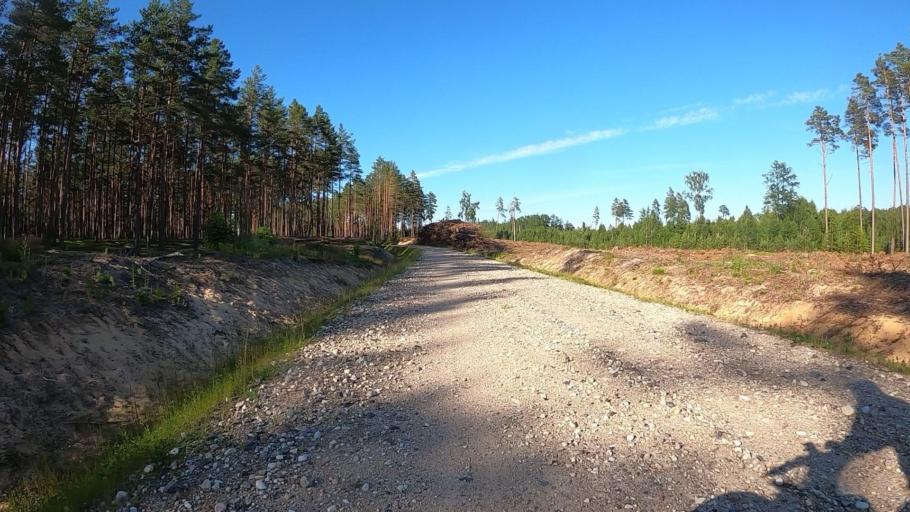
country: LV
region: Carnikava
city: Carnikava
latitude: 57.1078
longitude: 24.2513
